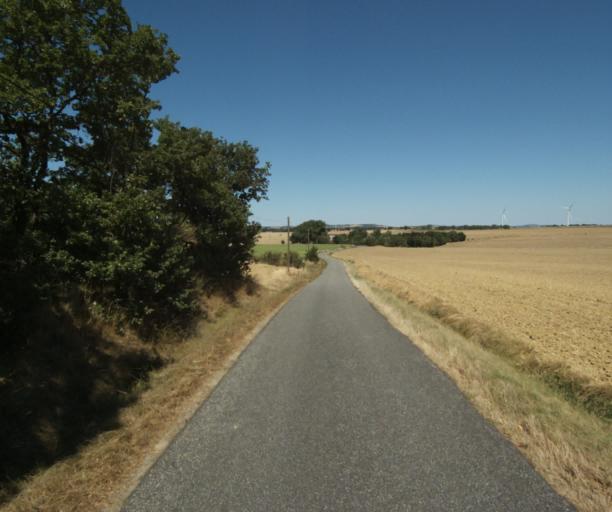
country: FR
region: Midi-Pyrenees
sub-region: Departement de la Haute-Garonne
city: Saint-Felix-Lauragais
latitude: 43.4588
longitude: 1.9041
